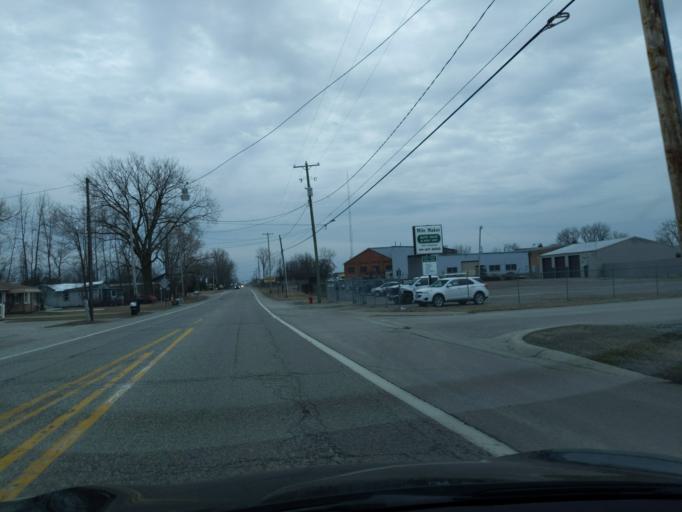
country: US
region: Michigan
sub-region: Bay County
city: Bay City
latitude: 43.6357
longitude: -83.9138
